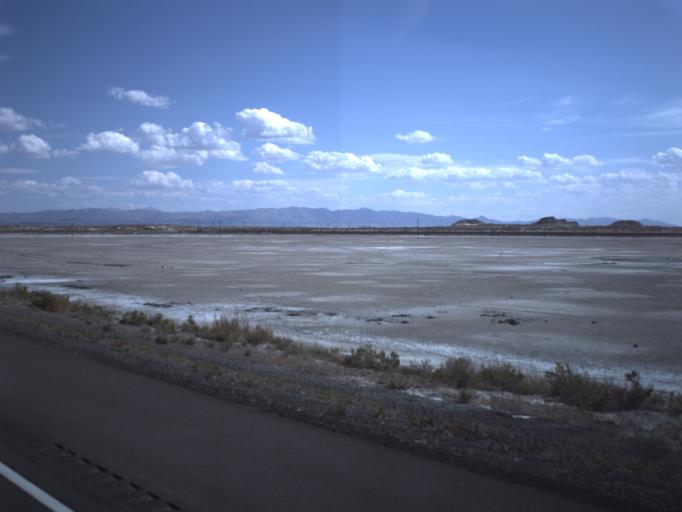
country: US
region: Utah
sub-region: Tooele County
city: Wendover
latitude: 40.7271
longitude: -113.2971
